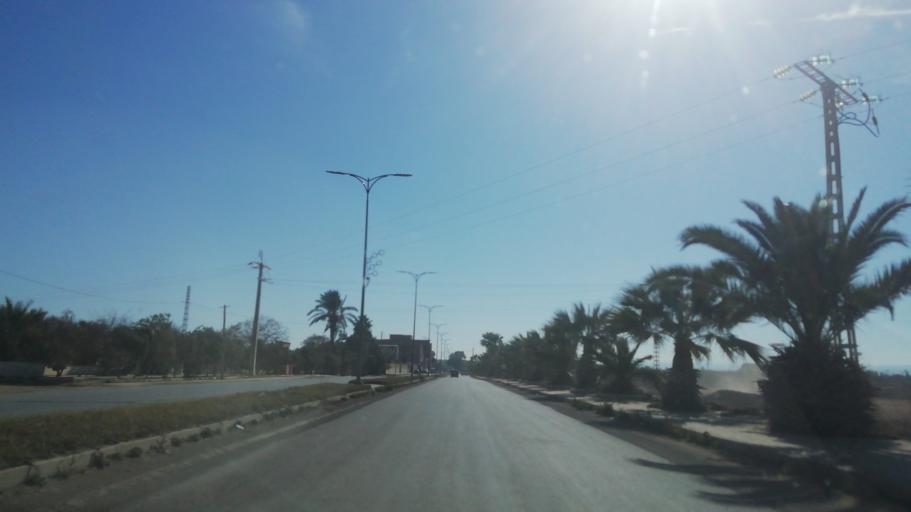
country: DZ
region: Oran
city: Es Senia
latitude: 35.6209
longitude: -0.5903
